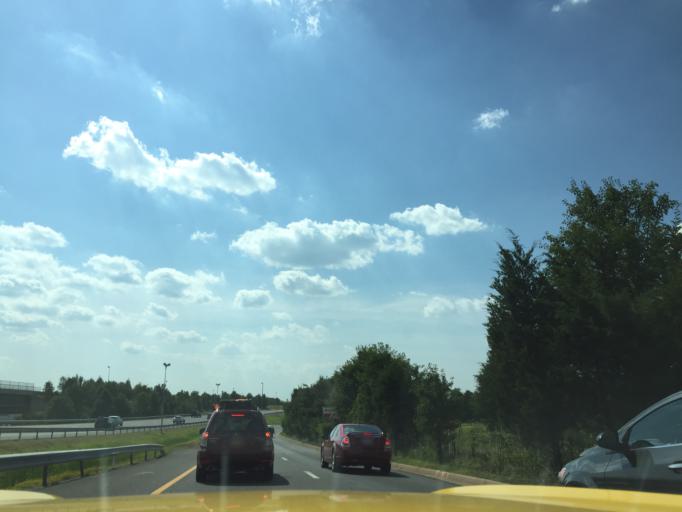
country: US
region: Virginia
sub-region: Fairfax County
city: Floris
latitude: 38.9629
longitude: -77.4219
